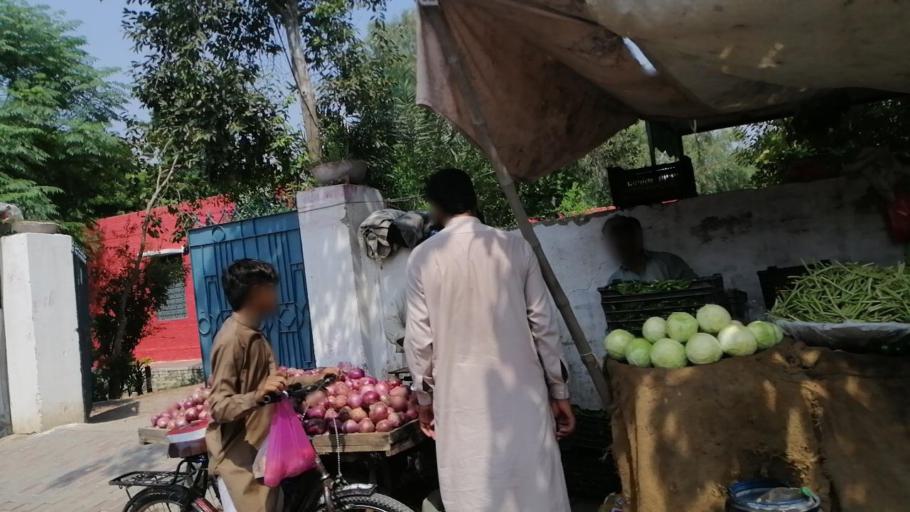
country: PK
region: Punjab
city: Kamalia
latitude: 30.7269
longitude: 72.6539
